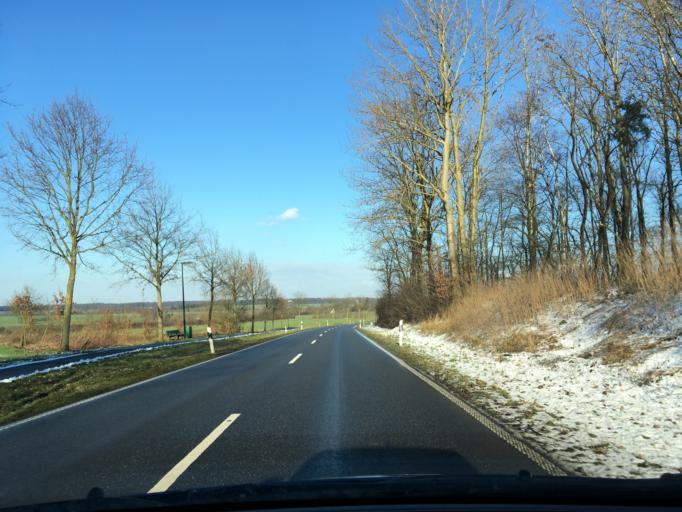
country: DE
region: Schleswig-Holstein
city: Krukow
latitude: 53.4353
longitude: 10.4726
